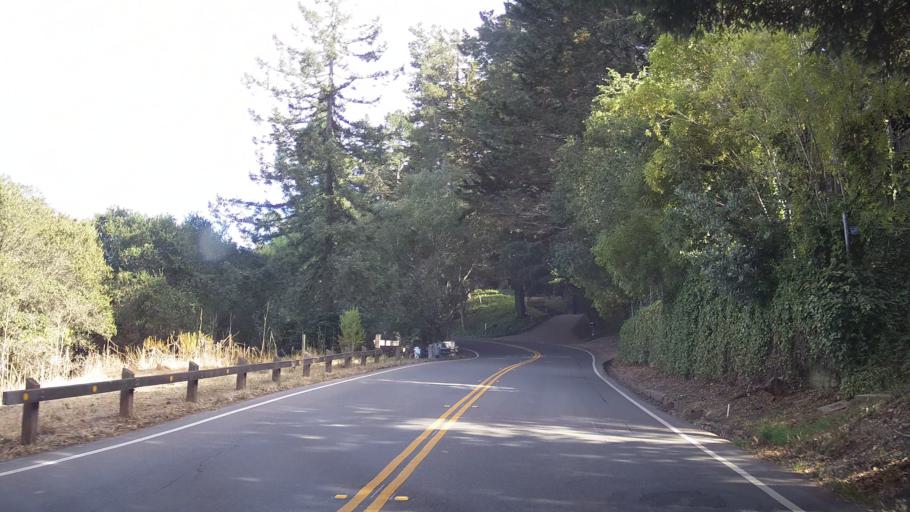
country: US
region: California
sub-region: Contra Costa County
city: Kensington
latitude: 37.9025
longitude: -122.2631
